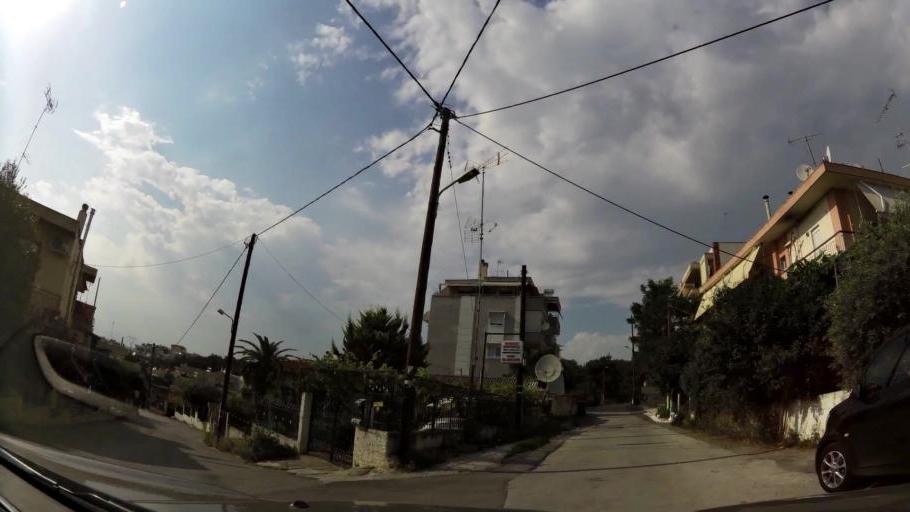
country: GR
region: Central Macedonia
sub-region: Nomos Thessalonikis
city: Polichni
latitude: 40.6608
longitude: 22.9584
